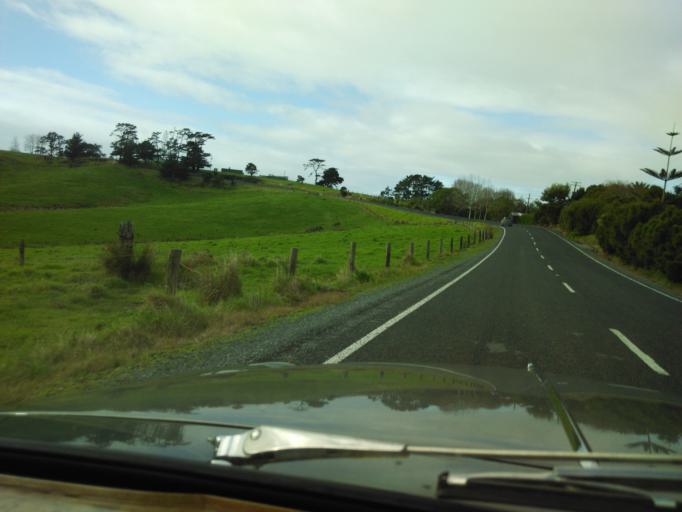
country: NZ
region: Auckland
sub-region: Auckland
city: Wellsford
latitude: -36.3356
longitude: 174.3958
